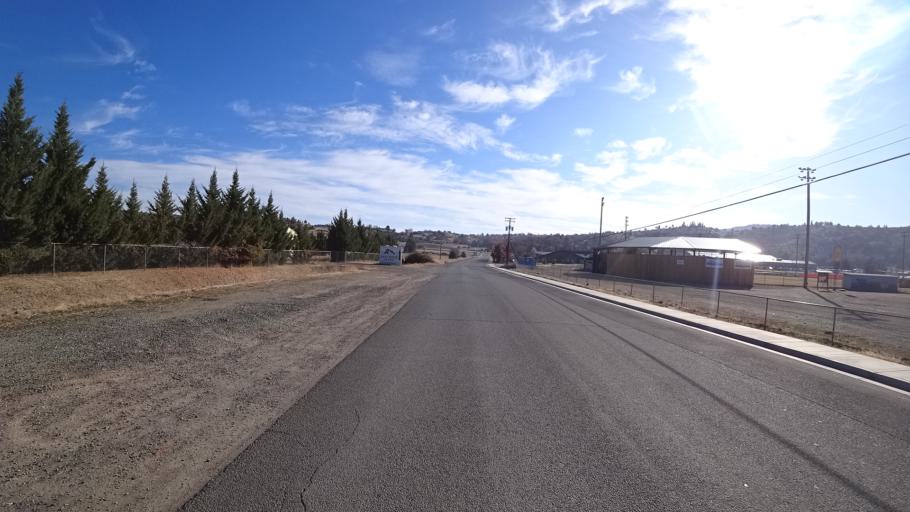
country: US
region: California
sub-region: Siskiyou County
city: Yreka
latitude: 41.7091
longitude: -122.6373
